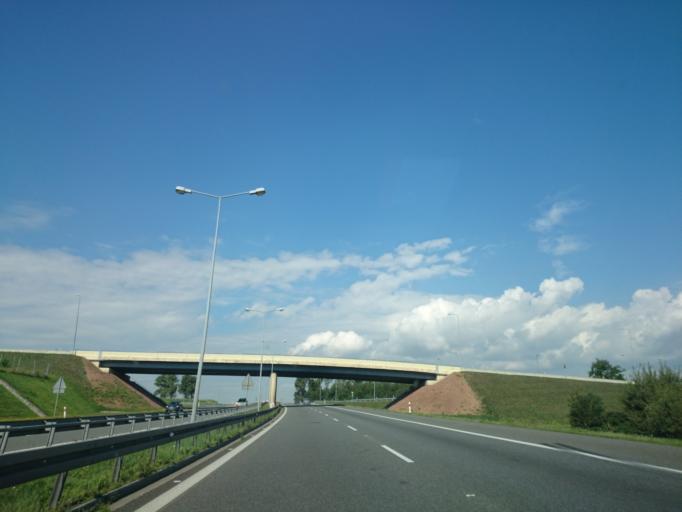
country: PL
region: Opole Voivodeship
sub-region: Powiat strzelecki
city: Ujazd
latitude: 50.4455
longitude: 18.3496
